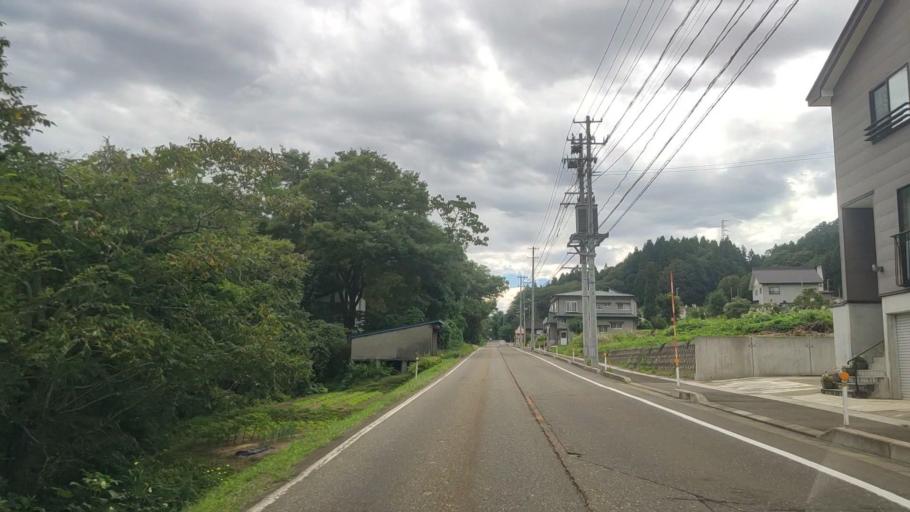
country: JP
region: Niigata
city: Arai
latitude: 36.9998
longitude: 138.2658
